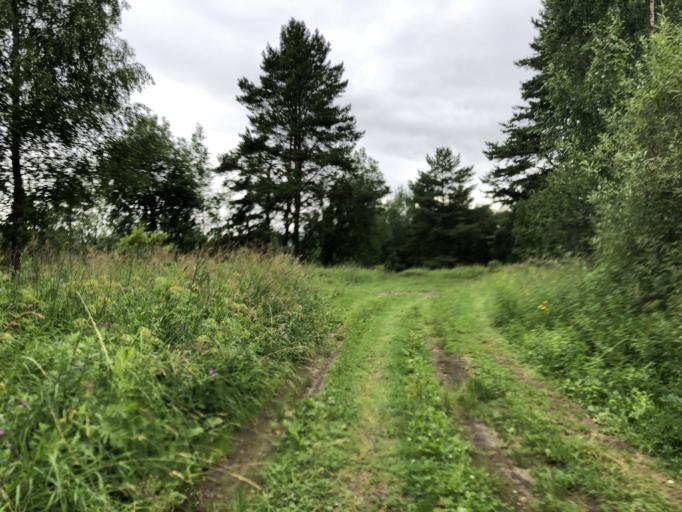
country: RU
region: Tverskaya
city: Rzhev
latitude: 56.2470
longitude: 34.3690
